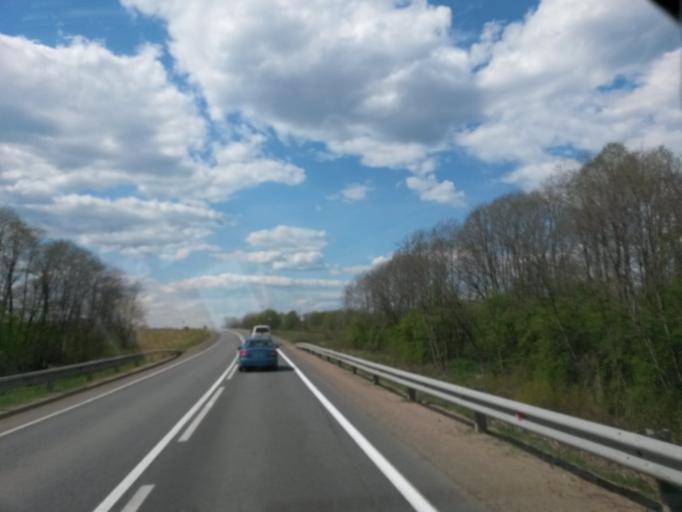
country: RU
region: Jaroslavl
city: Bol'shoye Selo
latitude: 57.7269
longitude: 38.9100
